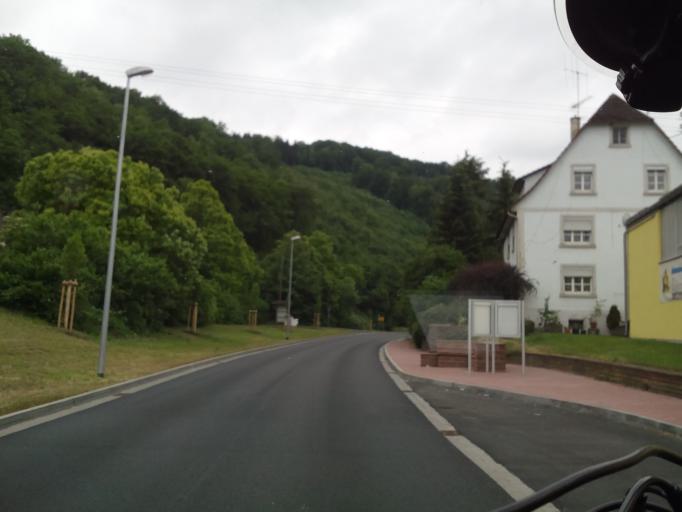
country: DE
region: Bavaria
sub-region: Regierungsbezirk Unterfranken
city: Kreuzwertheim
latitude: 49.7473
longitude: 9.5705
